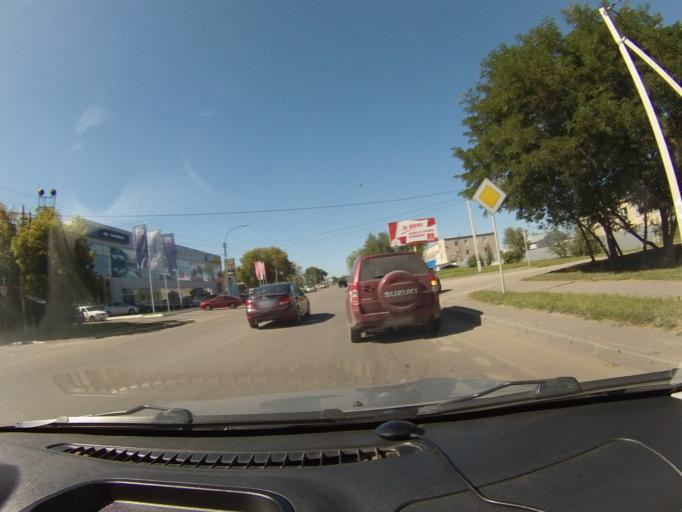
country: RU
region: Tambov
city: Donskoye
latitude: 52.7581
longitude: 41.4661
